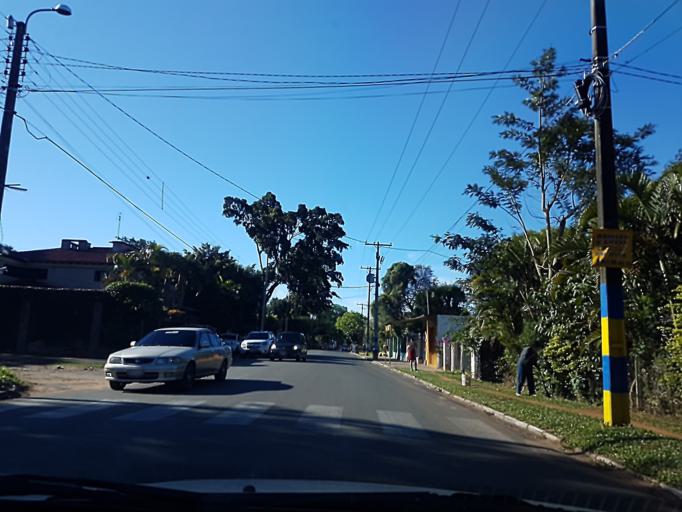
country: PY
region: Central
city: San Lorenzo
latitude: -25.2785
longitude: -57.4736
